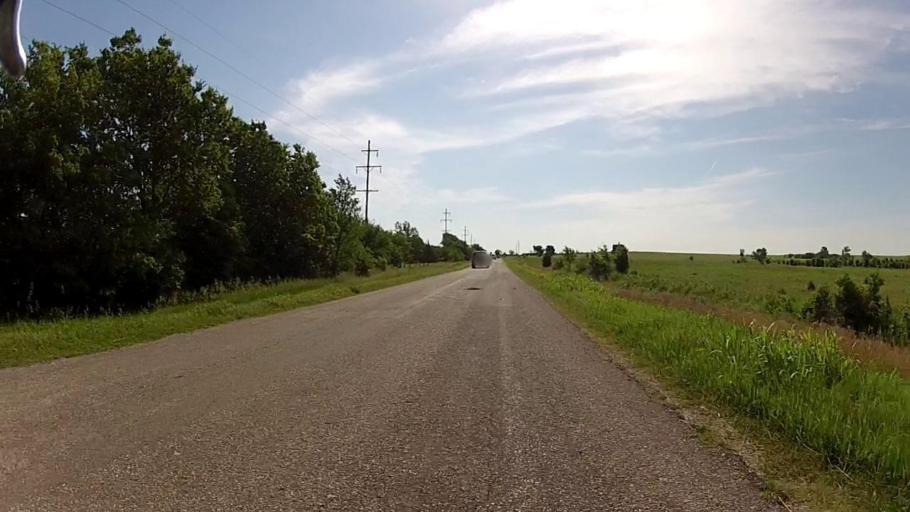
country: US
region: Kansas
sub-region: Cowley County
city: Winfield
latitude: 37.0710
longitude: -96.6641
